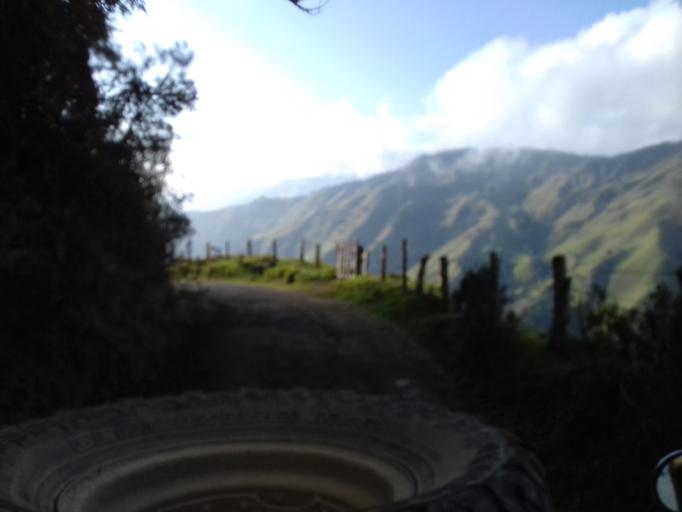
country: CO
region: Quindio
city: Salento
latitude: 4.5492
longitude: -75.4960
